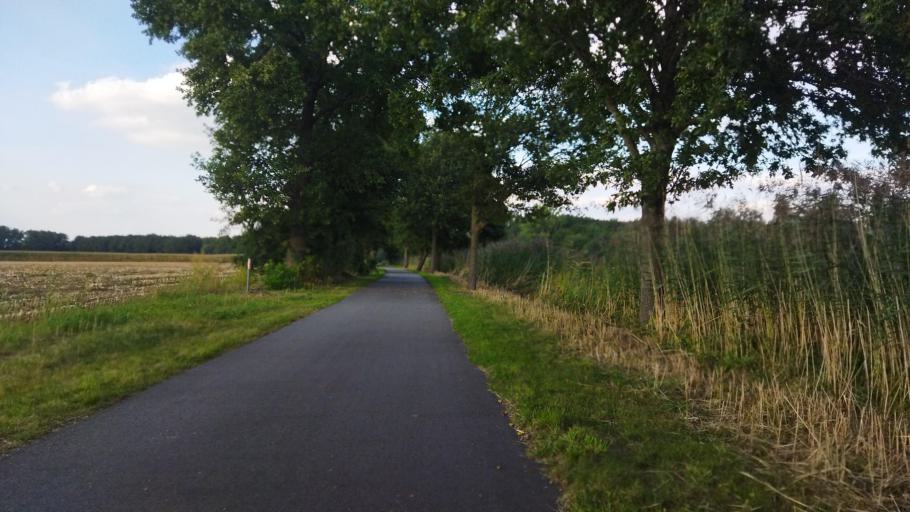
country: DE
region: Lower Saxony
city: Dersum
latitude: 52.9647
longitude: 7.3007
